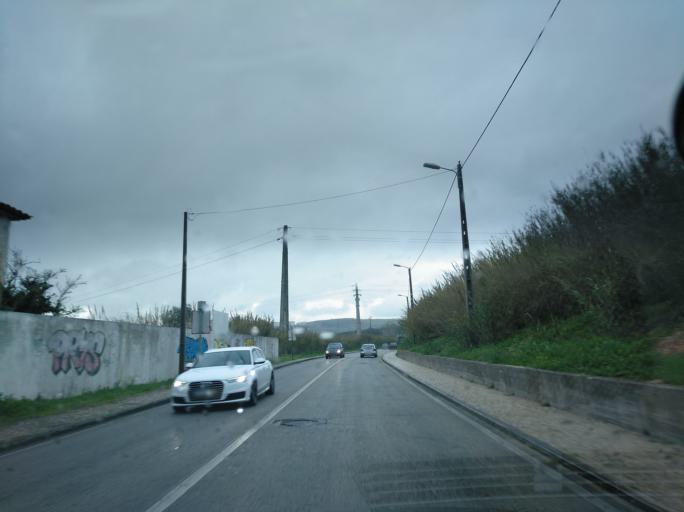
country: PT
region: Lisbon
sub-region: Odivelas
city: Pontinha
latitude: 38.7783
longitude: -9.1973
